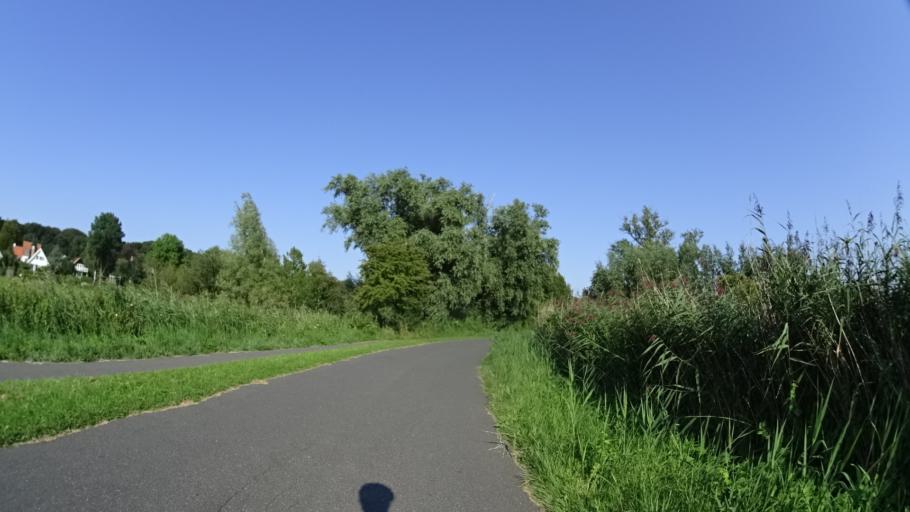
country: DK
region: Central Jutland
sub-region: Arhus Kommune
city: Stavtrup
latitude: 56.1478
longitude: 10.1245
